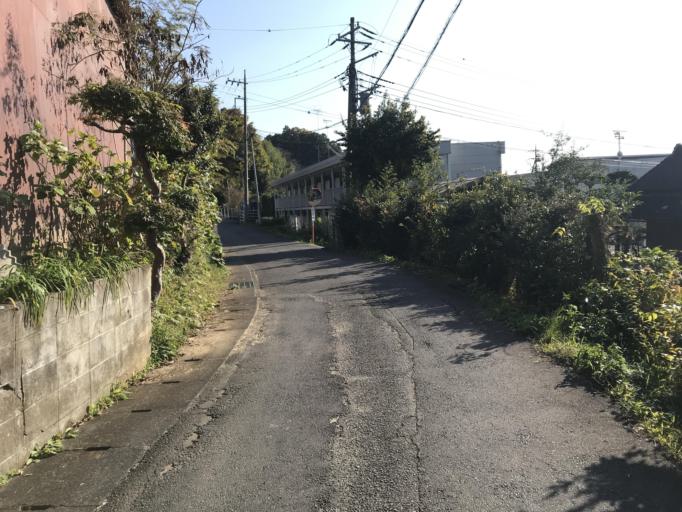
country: JP
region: Ibaraki
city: Ishioka
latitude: 36.1870
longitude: 140.2694
